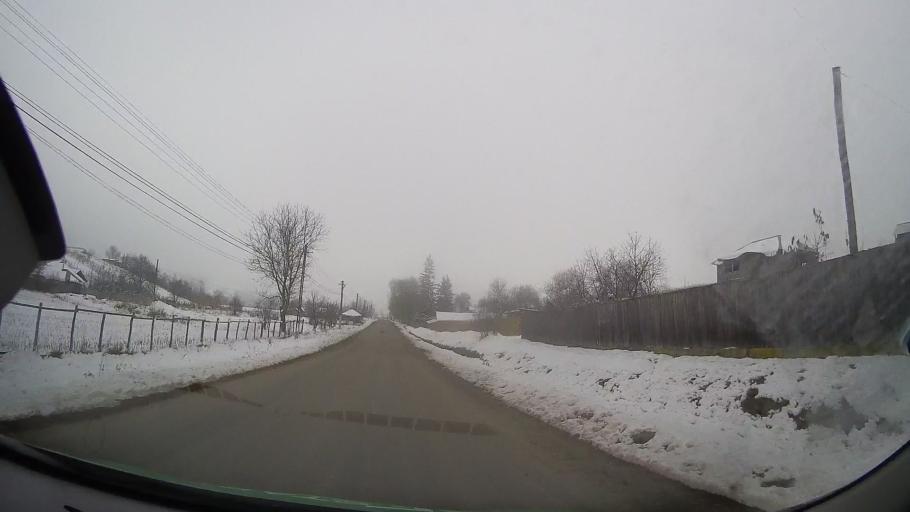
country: RO
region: Bacau
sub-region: Comuna Vultureni
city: Vultureni
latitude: 46.4007
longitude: 27.2732
